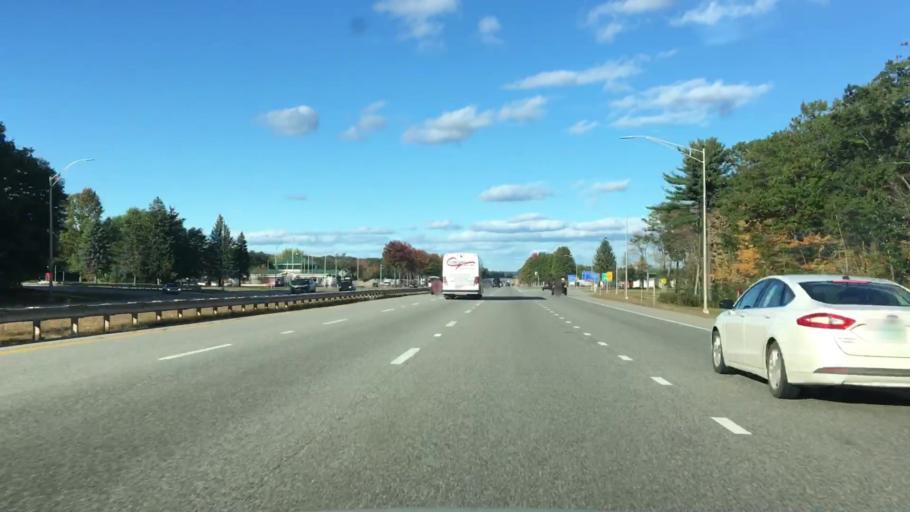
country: US
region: Maine
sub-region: York County
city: West Kennebunk
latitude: 43.4061
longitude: -70.5618
